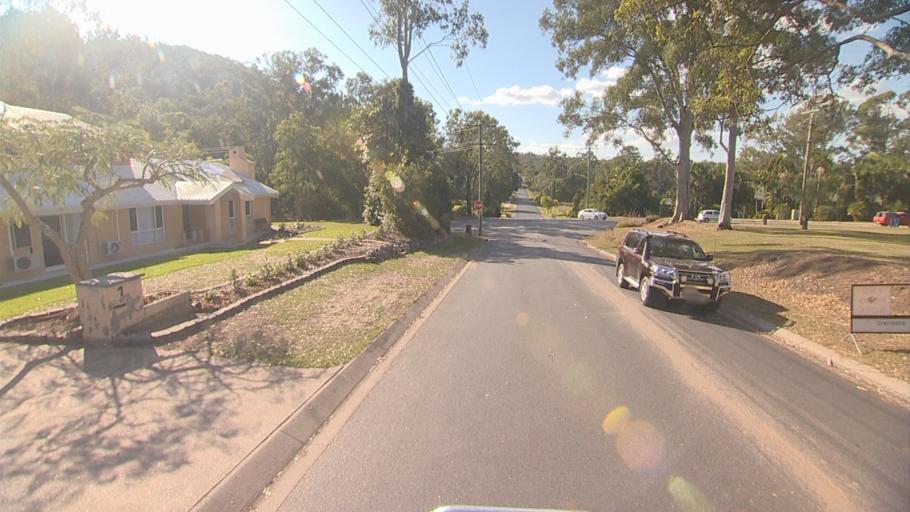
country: AU
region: Queensland
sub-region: Logan
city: Windaroo
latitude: -27.7423
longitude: 153.1853
